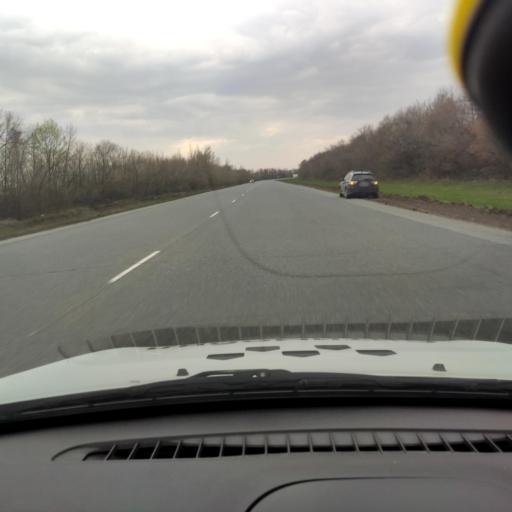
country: RU
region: Samara
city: Mezhdurechensk
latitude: 53.2684
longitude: 49.2832
